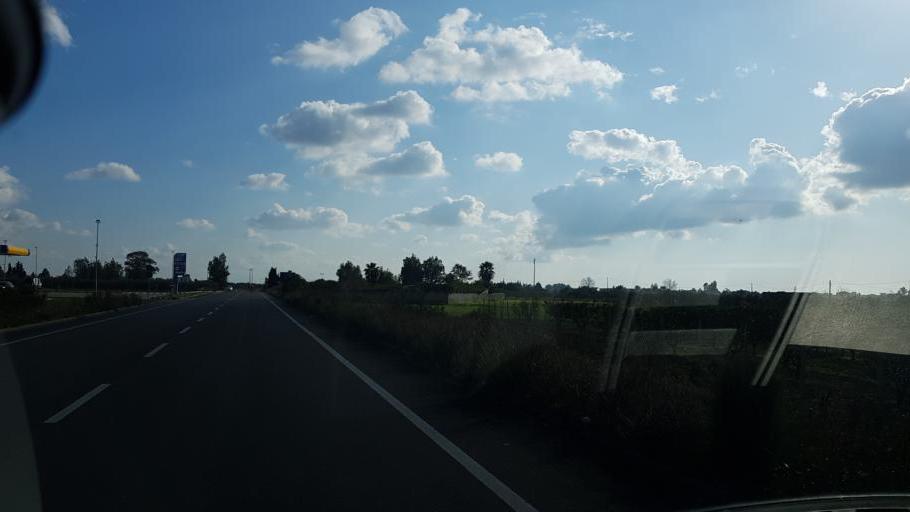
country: IT
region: Apulia
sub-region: Provincia di Lecce
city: Veglie
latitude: 40.3420
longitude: 17.9780
